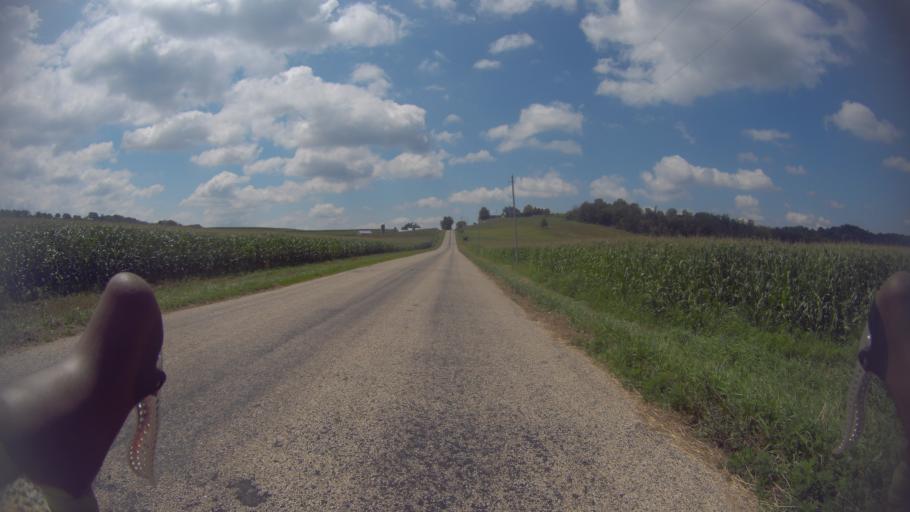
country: US
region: Wisconsin
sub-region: Sauk County
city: Sauk City
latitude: 43.2387
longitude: -89.6374
